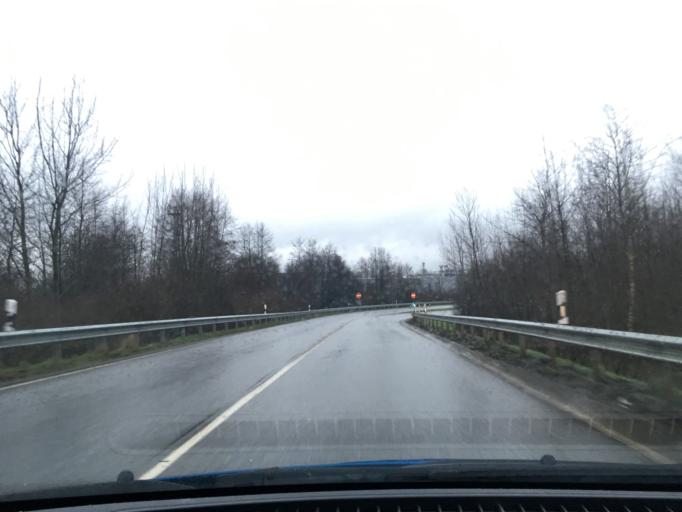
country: DE
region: Schleswig-Holstein
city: Ottenbuttel
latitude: 53.9577
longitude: 9.4888
